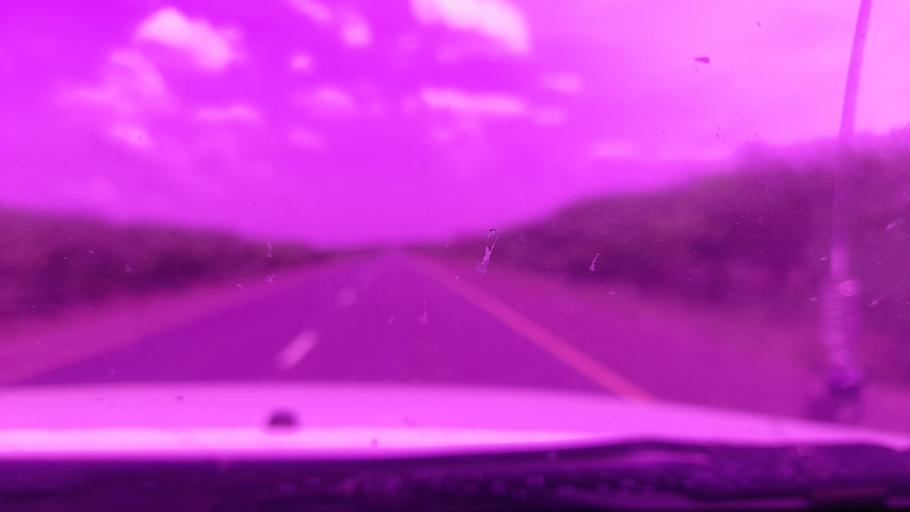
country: ET
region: Afar
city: Awash
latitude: 9.3608
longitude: 40.3059
